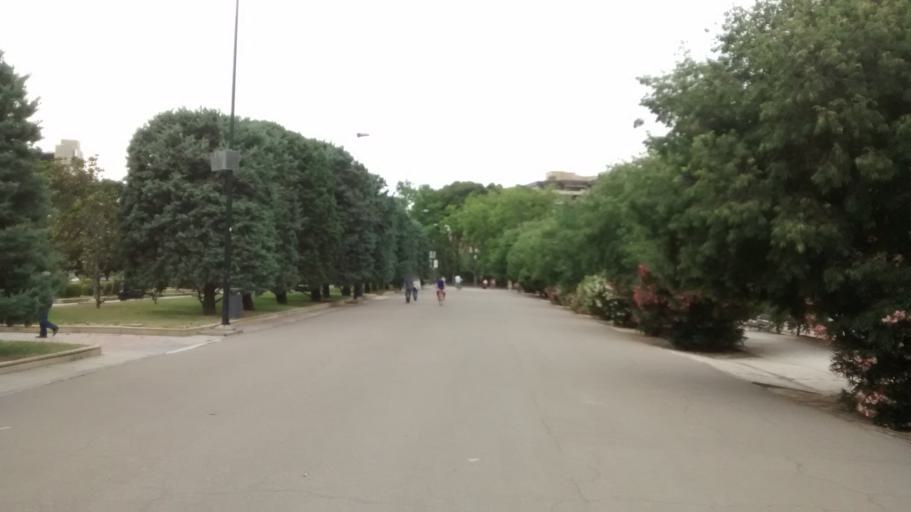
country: ES
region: Aragon
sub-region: Provincia de Zaragoza
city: Delicias
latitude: 41.6358
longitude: -0.8956
